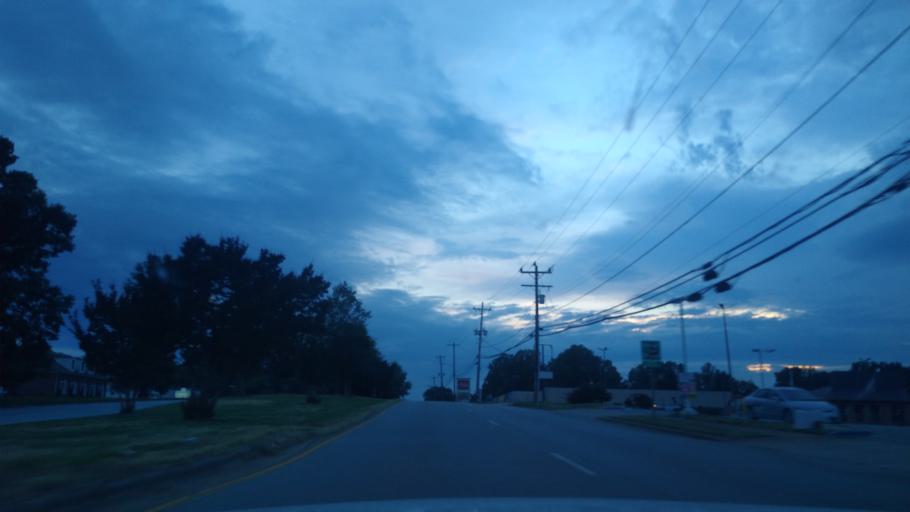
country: US
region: North Carolina
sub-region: Guilford County
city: Greensboro
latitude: 36.1133
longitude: -79.7651
